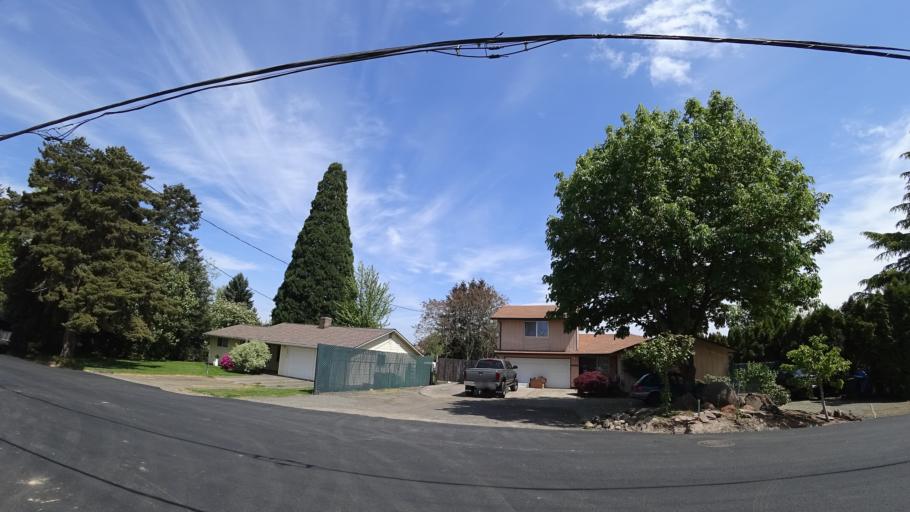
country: US
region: Oregon
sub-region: Washington County
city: Aloha
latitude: 45.4686
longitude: -122.8820
